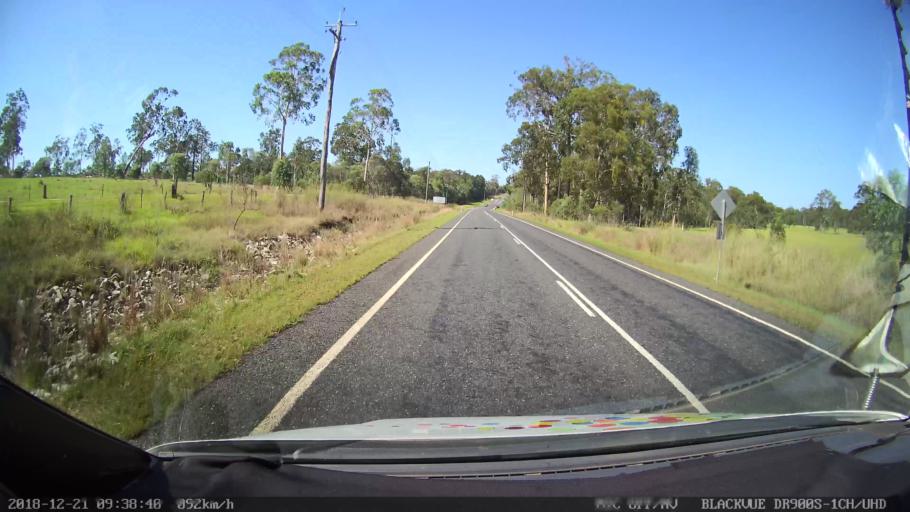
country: AU
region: New South Wales
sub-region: Clarence Valley
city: Grafton
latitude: -29.5525
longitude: 152.9808
